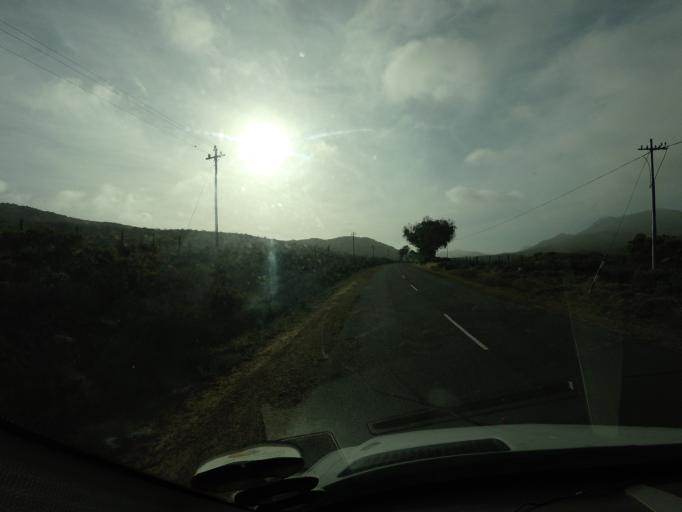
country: ZA
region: Western Cape
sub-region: City of Cape Town
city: Retreat
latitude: -34.2568
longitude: 18.4526
